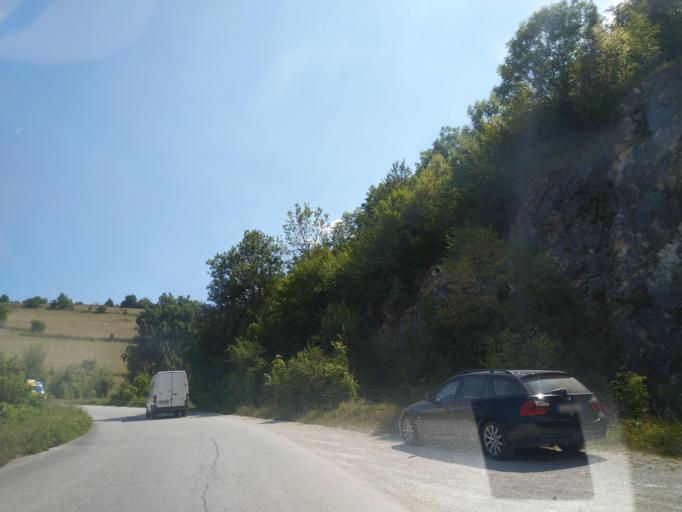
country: RS
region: Central Serbia
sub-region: Zlatiborski Okrug
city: Nova Varos
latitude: 43.4203
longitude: 19.9353
